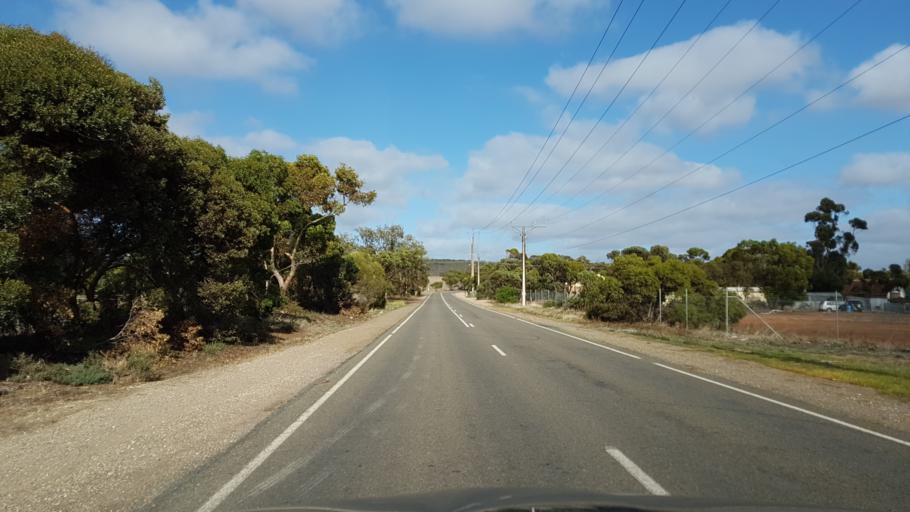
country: AU
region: South Australia
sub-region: Murray Bridge
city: Murray Bridge
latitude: -35.1174
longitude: 139.2430
